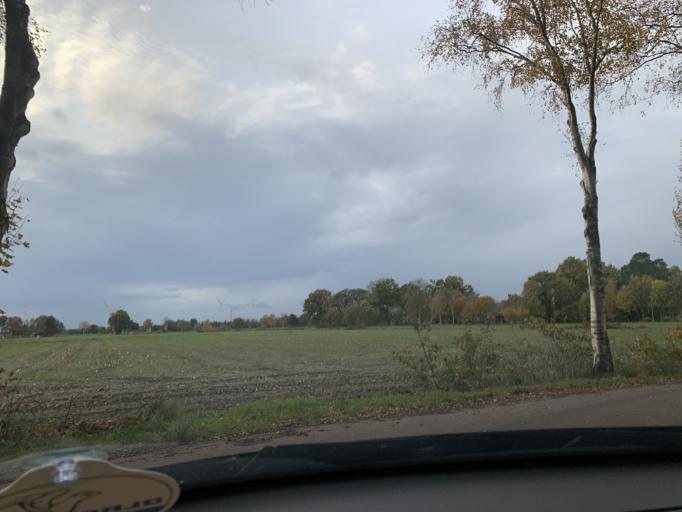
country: DE
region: Lower Saxony
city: Wiefelstede
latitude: 53.2630
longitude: 8.0676
